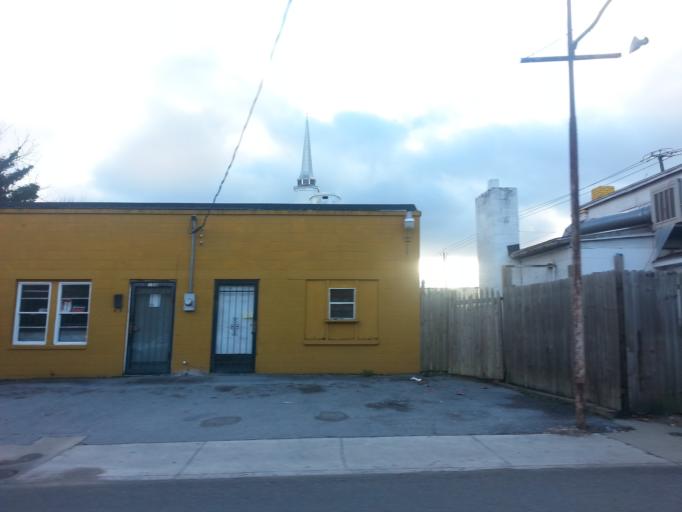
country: US
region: Tennessee
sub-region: Knox County
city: Knoxville
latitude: 35.9983
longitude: -83.8762
